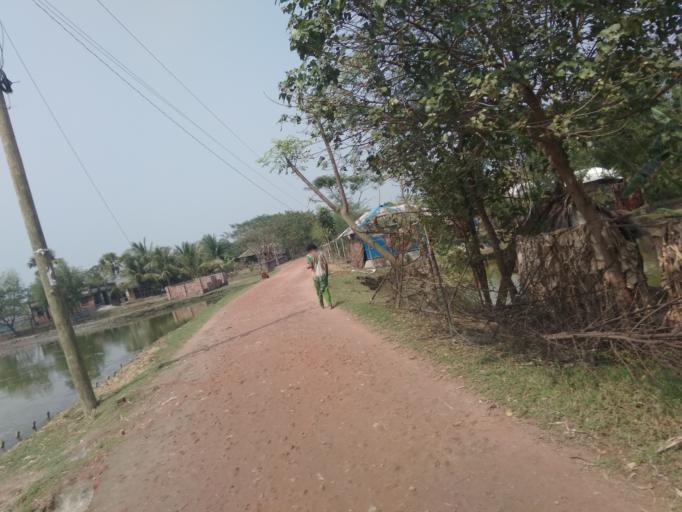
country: IN
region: West Bengal
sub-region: North 24 Parganas
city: Taki
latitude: 22.3005
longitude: 89.2684
